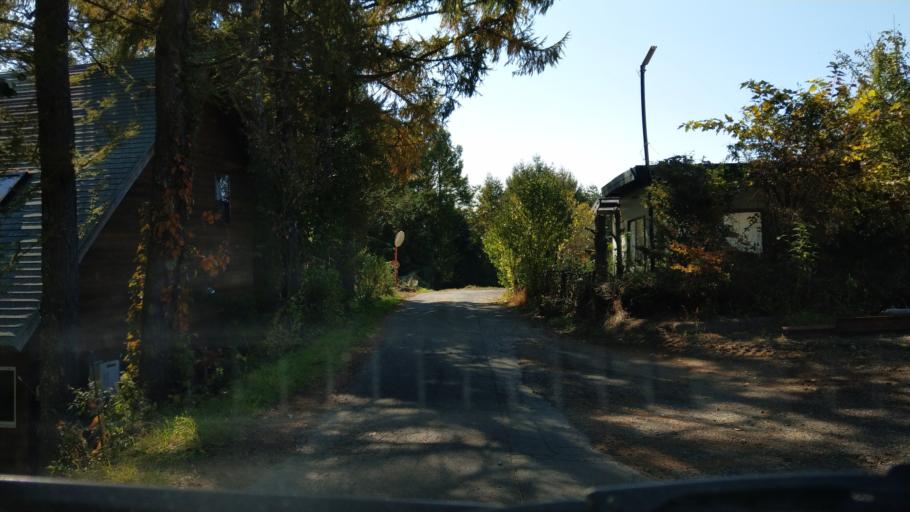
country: JP
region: Nagano
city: Komoro
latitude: 36.3584
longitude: 138.4495
